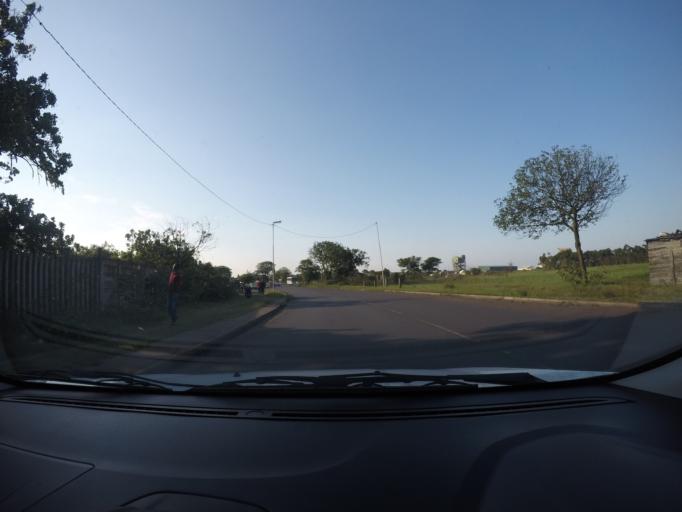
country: ZA
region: KwaZulu-Natal
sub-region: uThungulu District Municipality
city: Richards Bay
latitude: -28.7666
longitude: 32.0092
